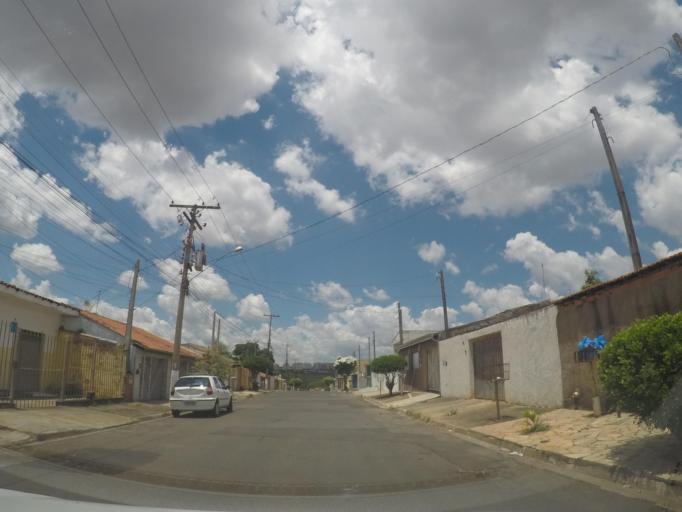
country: BR
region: Sao Paulo
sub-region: Hortolandia
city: Hortolandia
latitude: -22.8197
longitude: -47.2029
